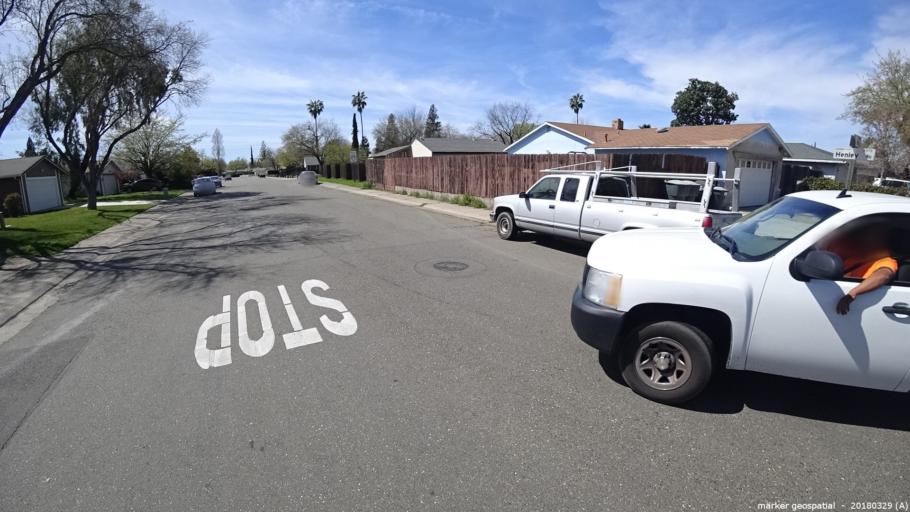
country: US
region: California
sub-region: Sacramento County
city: Rosemont
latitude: 38.5447
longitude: -121.3492
